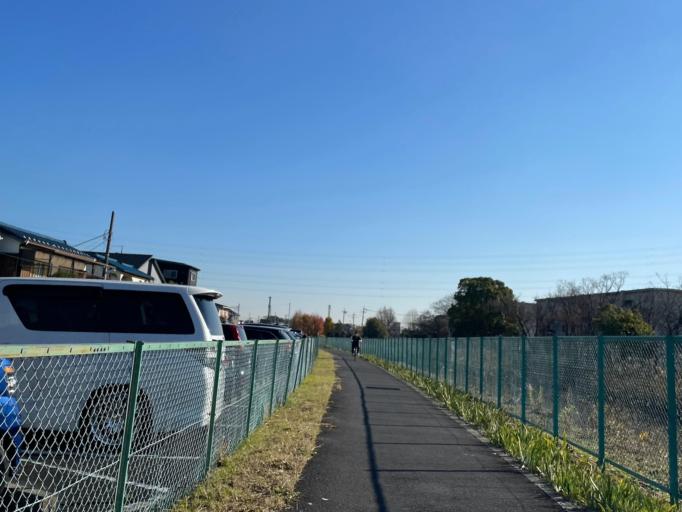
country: JP
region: Saitama
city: Soka
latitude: 35.8083
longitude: 139.8124
